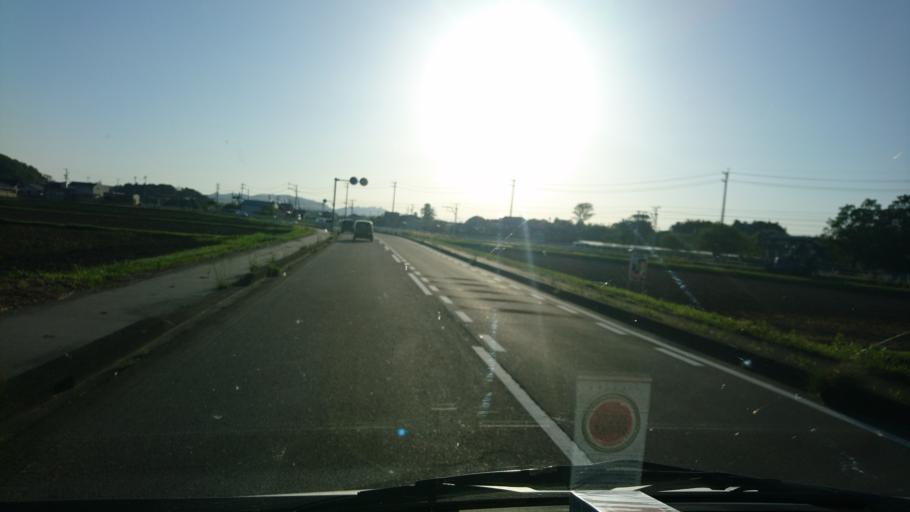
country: JP
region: Gifu
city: Mitake
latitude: 35.4282
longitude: 137.0794
